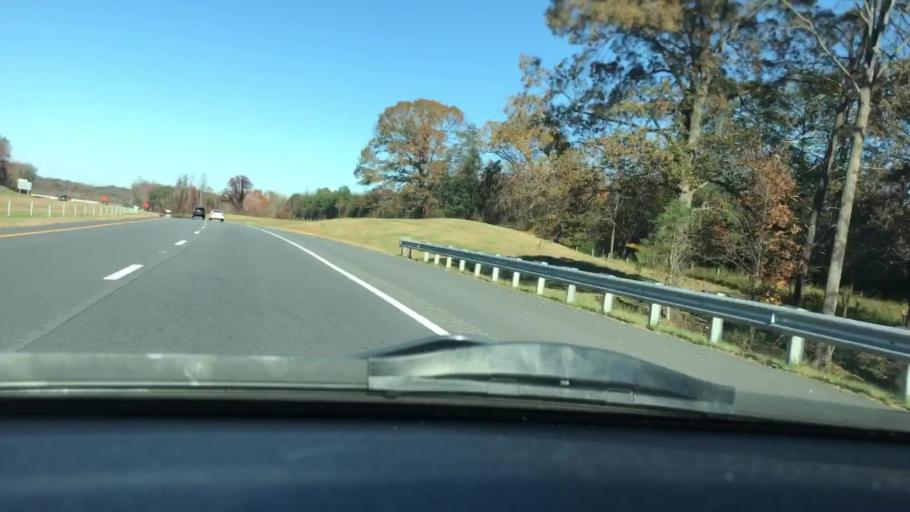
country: US
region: North Carolina
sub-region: Guilford County
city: Summerfield
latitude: 36.2161
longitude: -79.9170
